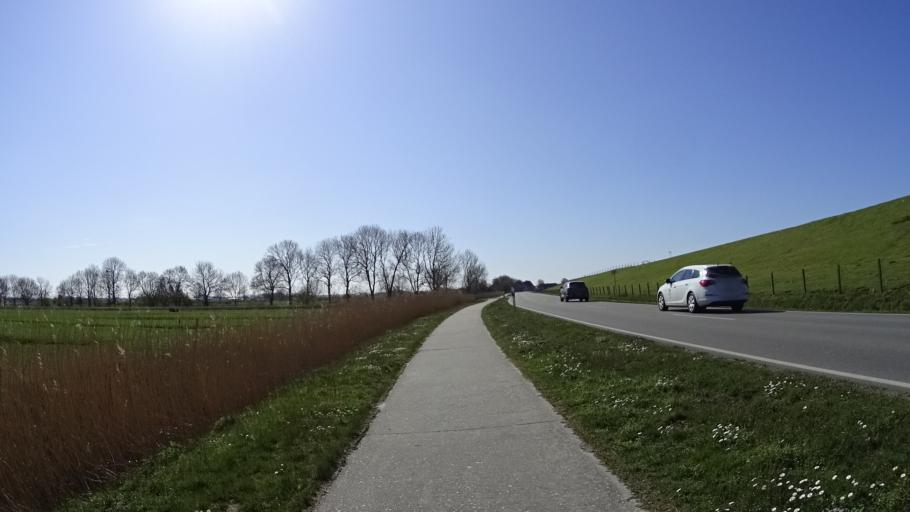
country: DE
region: Lower Saxony
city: Jemgum
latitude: 53.2480
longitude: 7.4066
